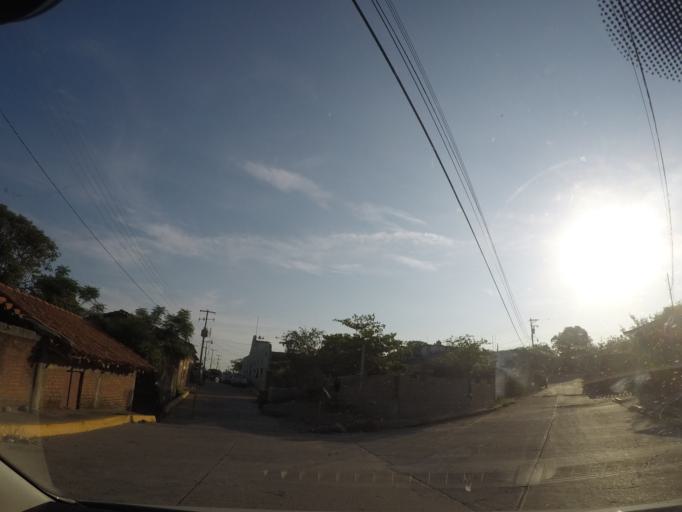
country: MX
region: Oaxaca
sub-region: Santo Domingo Tehuantepec
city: La Noria
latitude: 16.2431
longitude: -95.1532
